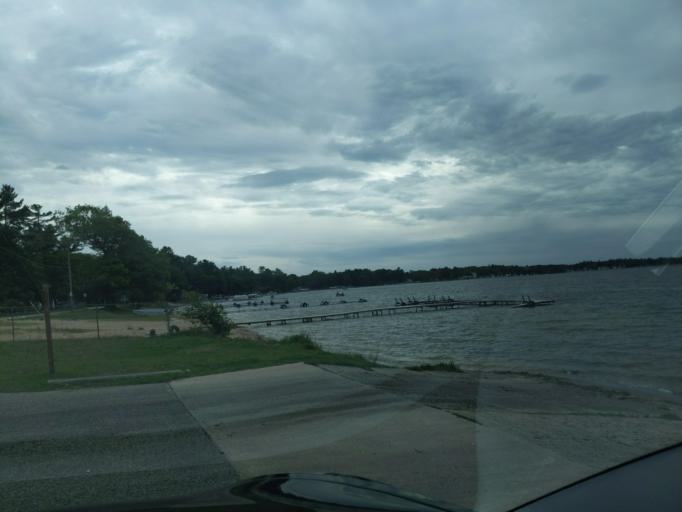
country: US
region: Michigan
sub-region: Wexford County
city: Cadillac
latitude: 44.2377
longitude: -85.4562
